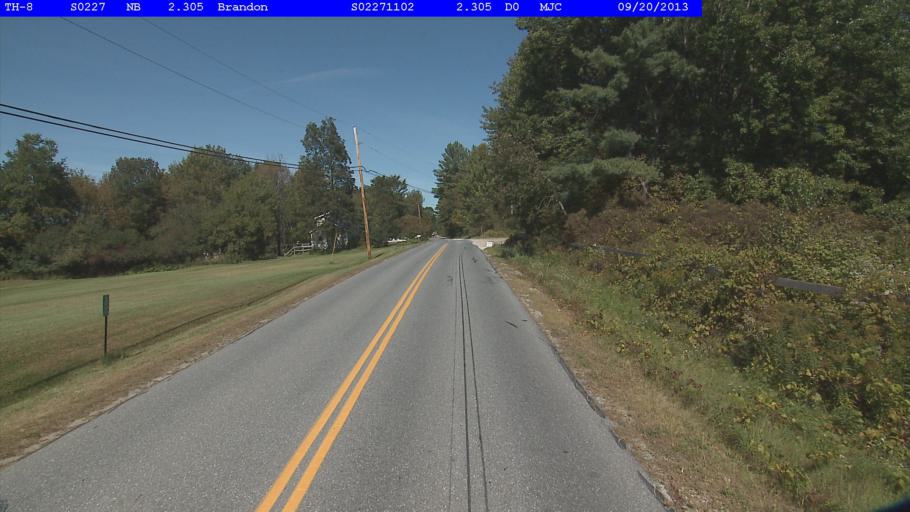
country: US
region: Vermont
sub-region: Rutland County
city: Brandon
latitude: 43.8076
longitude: -73.0565
